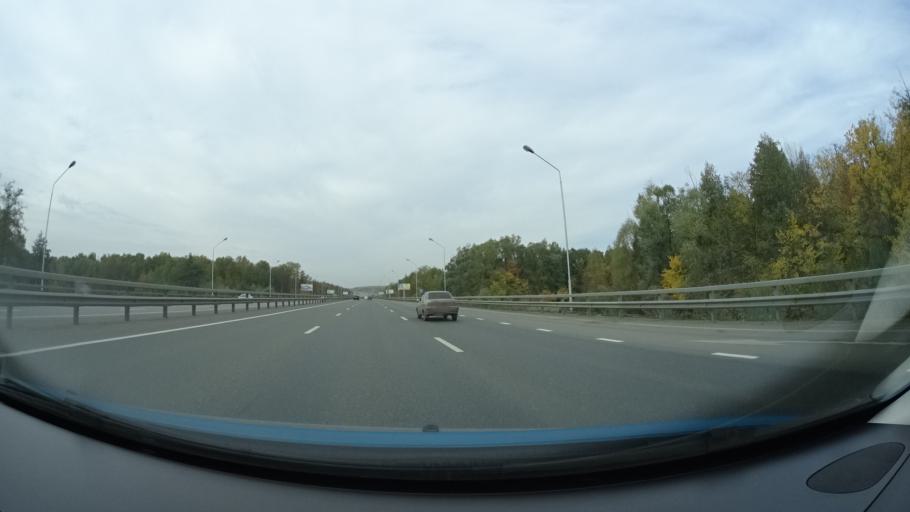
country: RU
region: Bashkortostan
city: Avdon
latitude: 54.6709
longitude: 55.8363
